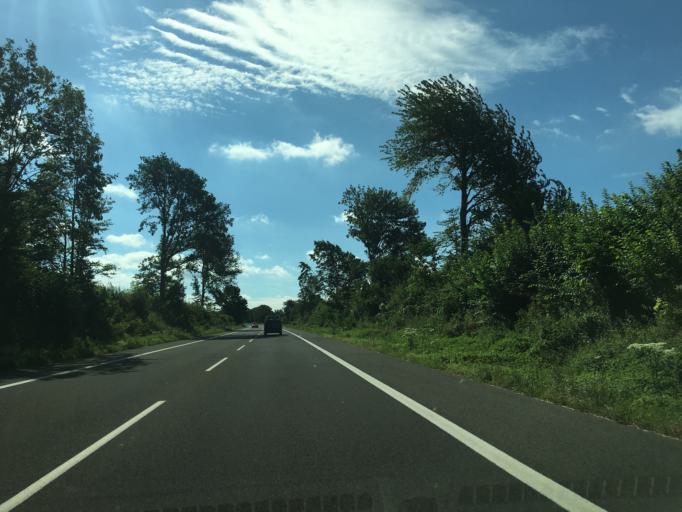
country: DE
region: North Rhine-Westphalia
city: Julich
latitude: 50.9716
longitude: 6.3549
